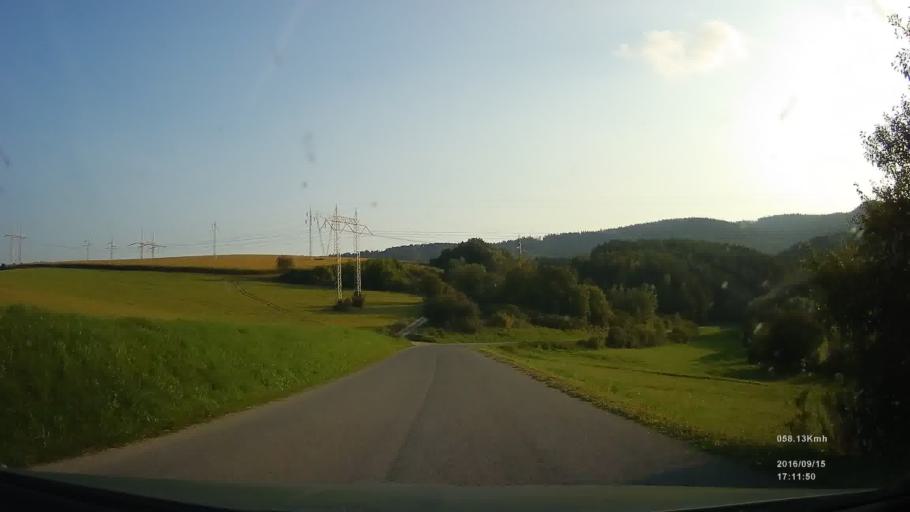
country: SK
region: Presovsky
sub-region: Okres Presov
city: Presov
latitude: 48.9159
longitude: 21.1010
